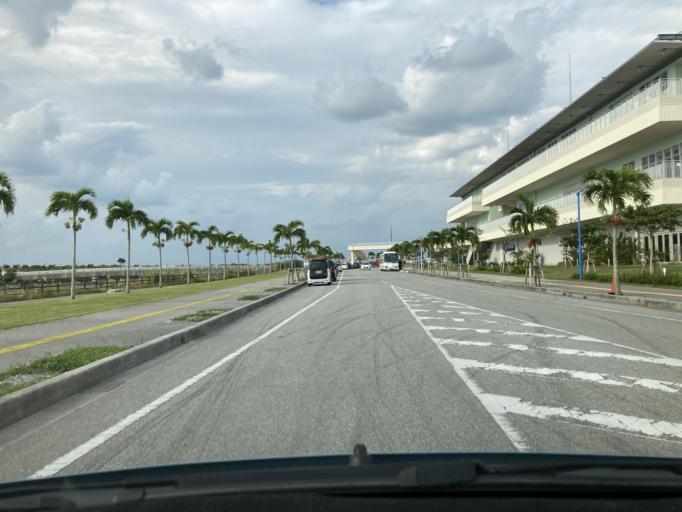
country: JP
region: Okinawa
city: Itoman
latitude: 26.1563
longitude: 127.6500
